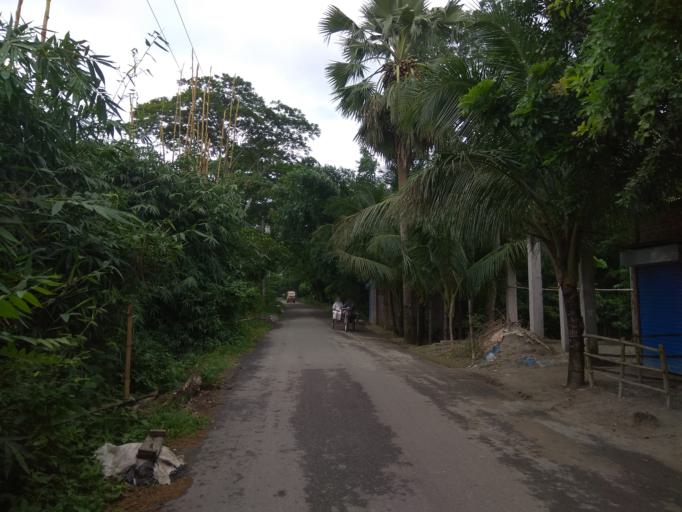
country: BD
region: Dhaka
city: Dohar
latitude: 23.4202
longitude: 90.0673
